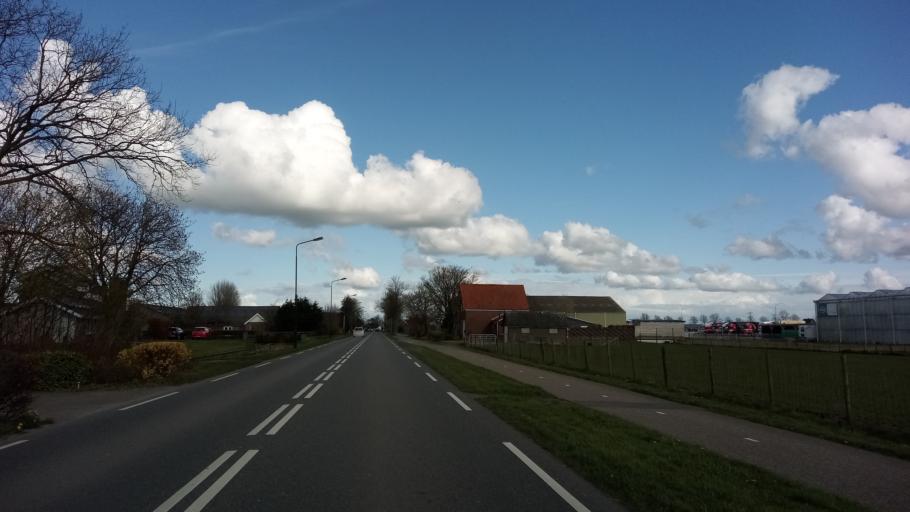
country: NL
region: North Holland
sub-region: Gemeente Heerhugowaard
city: Heerhugowaard
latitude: 52.6975
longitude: 4.8449
